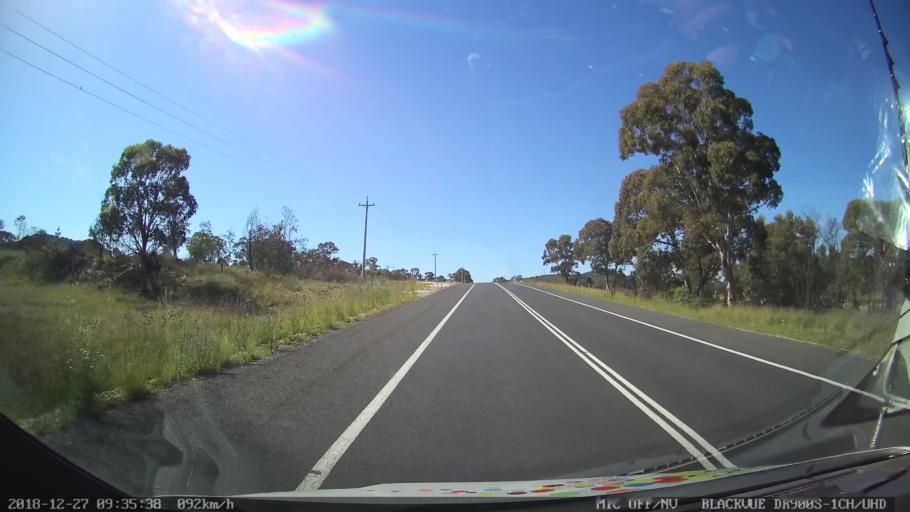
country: AU
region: New South Wales
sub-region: Lithgow
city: Portland
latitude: -33.2411
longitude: 150.0317
